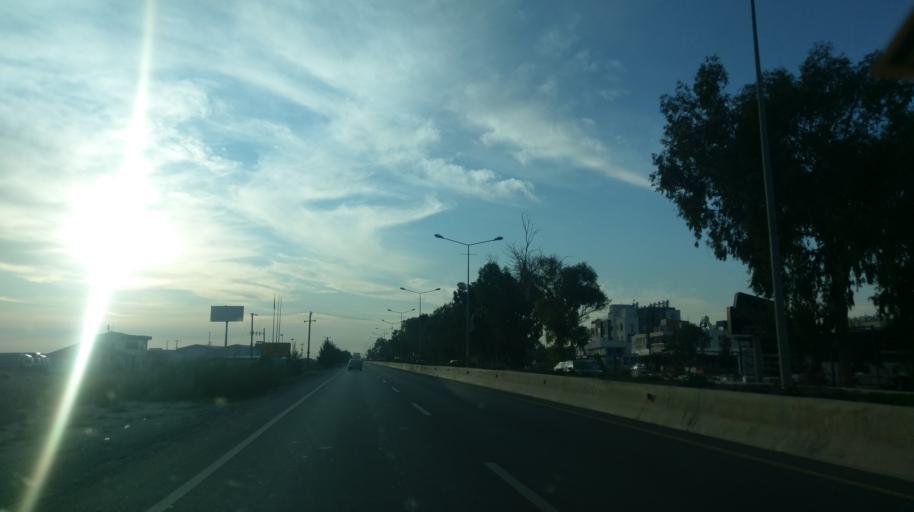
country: CY
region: Lefkosia
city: Nicosia
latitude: 35.2205
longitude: 33.4751
